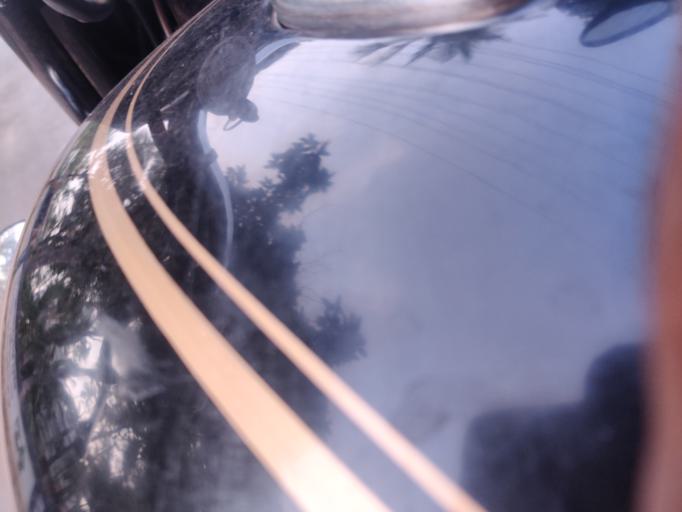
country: IN
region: Kerala
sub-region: Kozhikode
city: Mavoor
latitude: 11.2621
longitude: 75.9506
